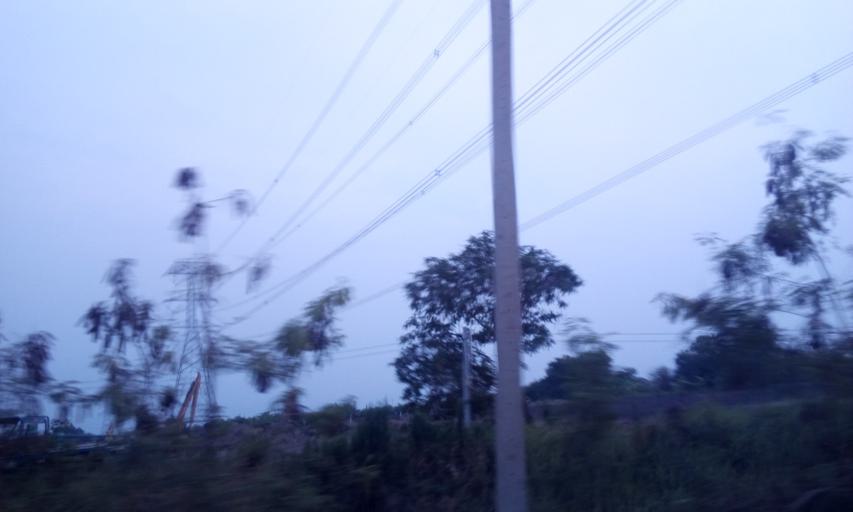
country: TH
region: Chachoengsao
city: Ban Pho
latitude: 13.6008
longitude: 101.1612
